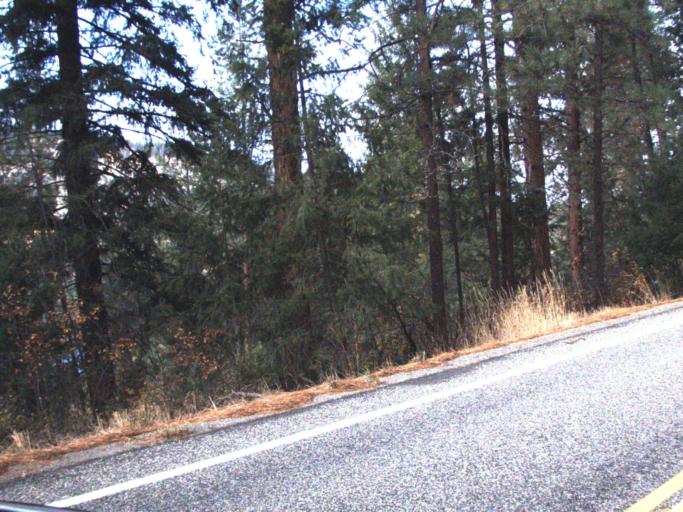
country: US
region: Washington
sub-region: Stevens County
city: Kettle Falls
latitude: 48.7647
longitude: -118.0325
